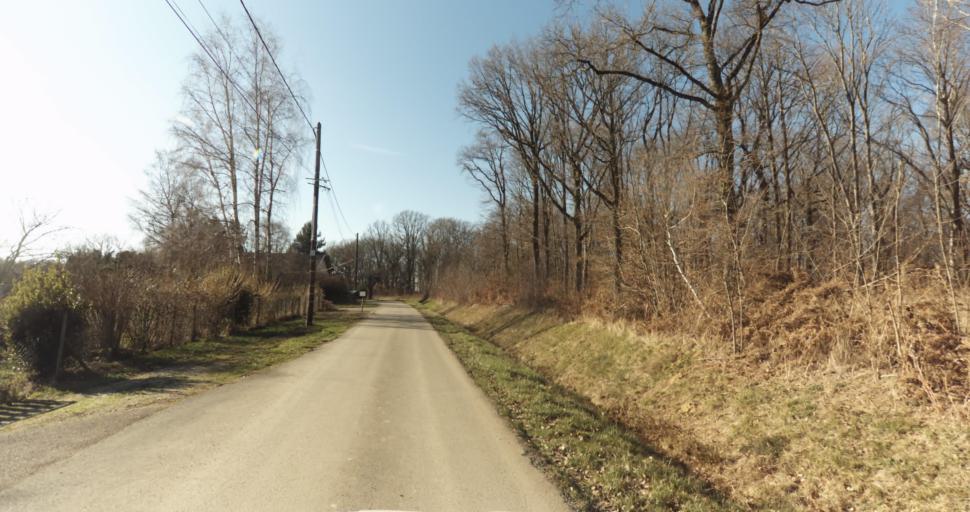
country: FR
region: Franche-Comte
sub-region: Departement du Jura
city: Montmorot
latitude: 46.6888
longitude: 5.4976
